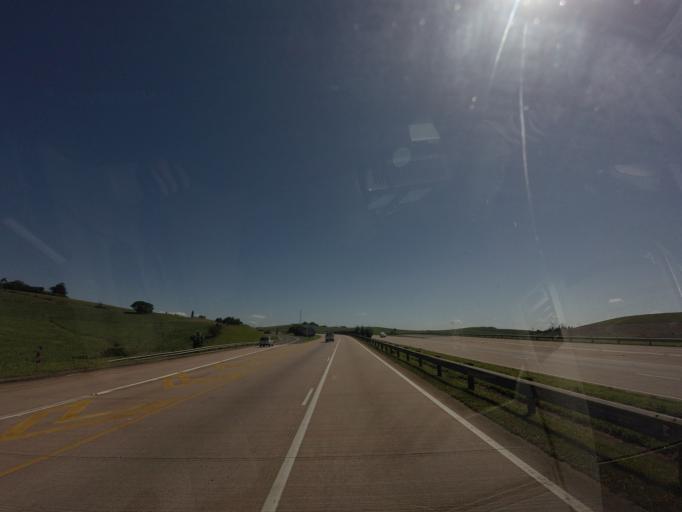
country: ZA
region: KwaZulu-Natal
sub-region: iLembe District Municipality
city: Stanger
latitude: -29.4333
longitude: 31.2706
